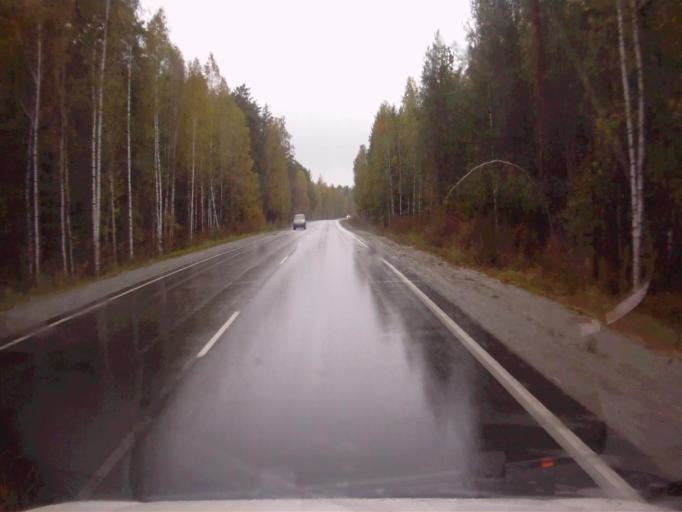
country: RU
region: Chelyabinsk
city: Kyshtym
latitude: 55.6518
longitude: 60.5783
